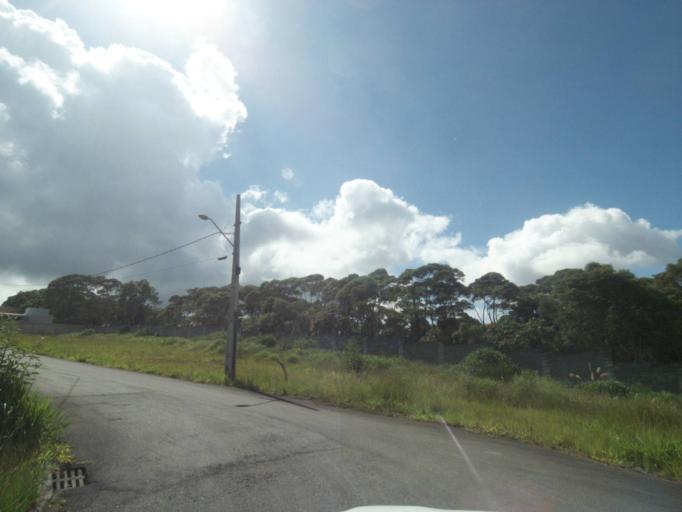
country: BR
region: Parana
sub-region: Colombo
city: Colombo
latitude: -25.3139
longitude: -49.2354
